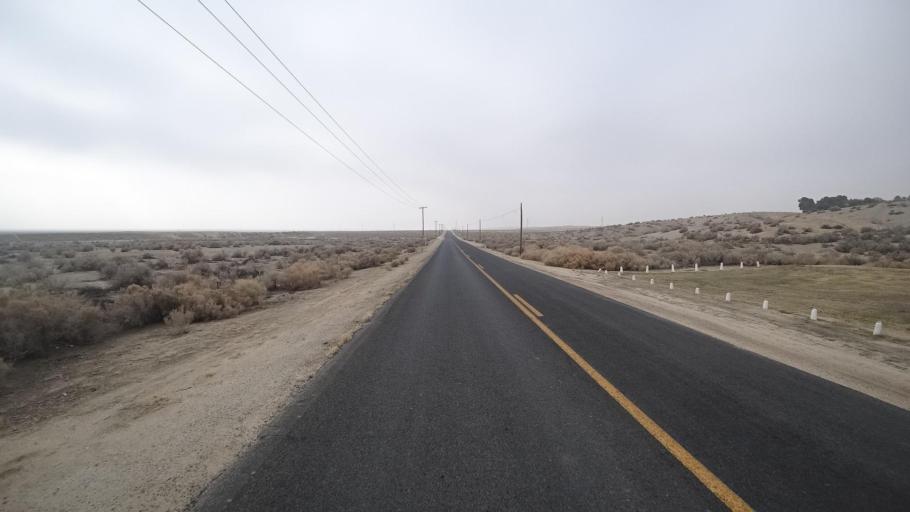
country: US
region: California
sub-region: Kern County
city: Ford City
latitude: 35.2344
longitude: -119.3299
